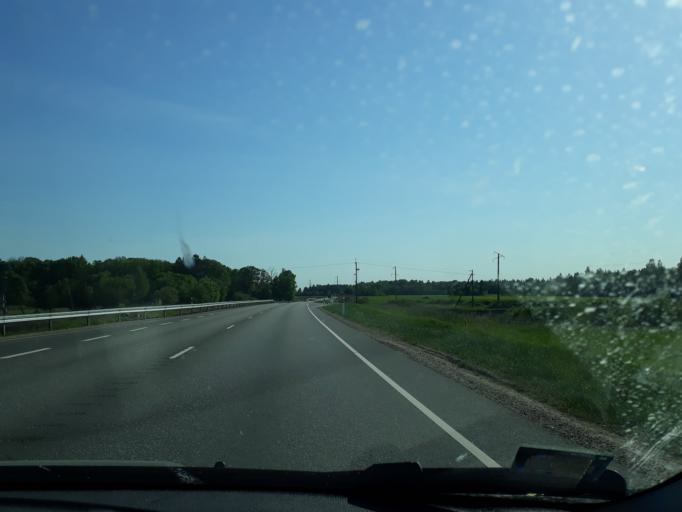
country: EE
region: Paernumaa
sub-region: Tootsi vald
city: Tootsi
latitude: 58.5783
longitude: 24.8879
